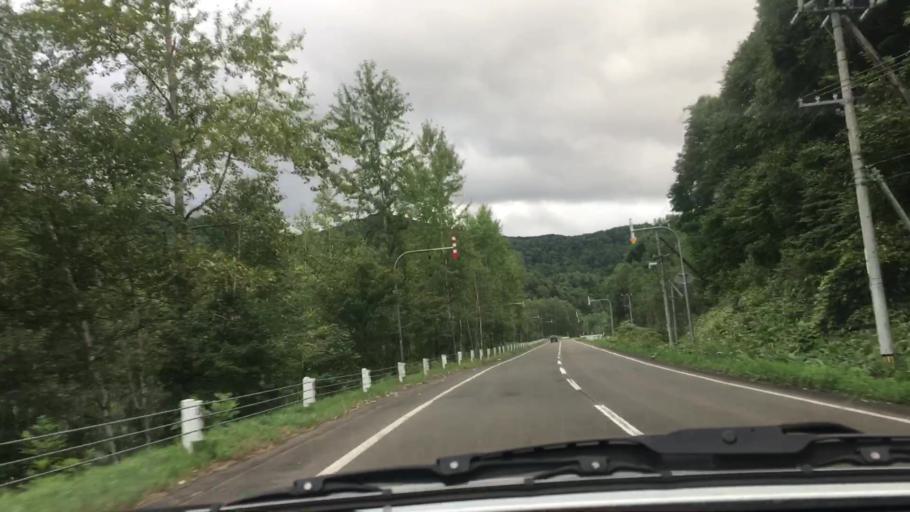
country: JP
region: Hokkaido
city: Shimo-furano
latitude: 43.0535
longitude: 142.5328
